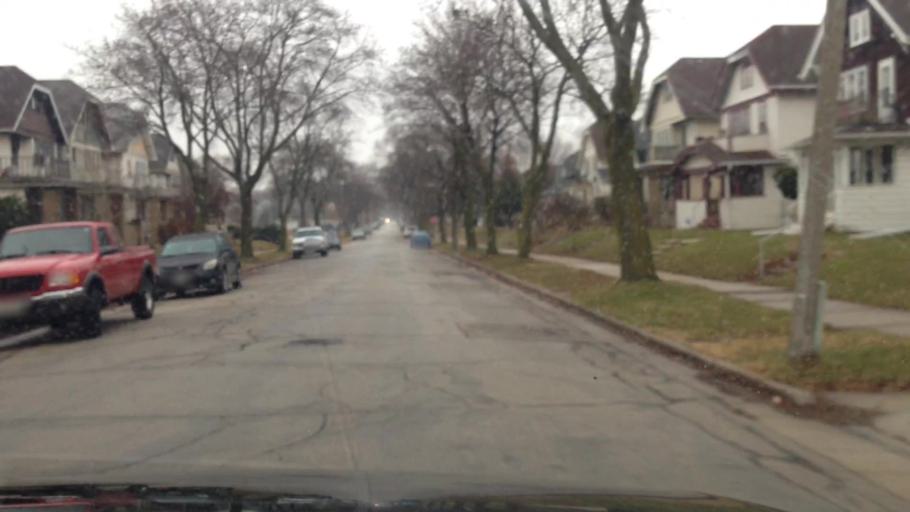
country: US
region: Wisconsin
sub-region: Milwaukee County
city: Shorewood
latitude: 43.0793
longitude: -87.9002
